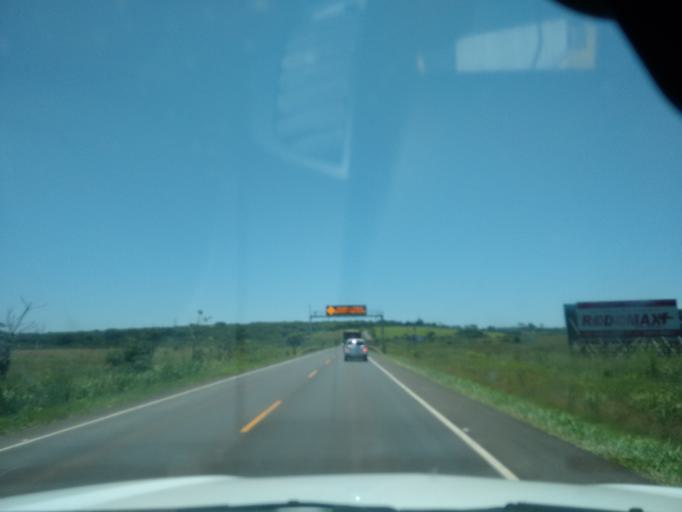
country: PY
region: Canindeyu
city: Salto del Guaira
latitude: -24.0425
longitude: -54.2761
